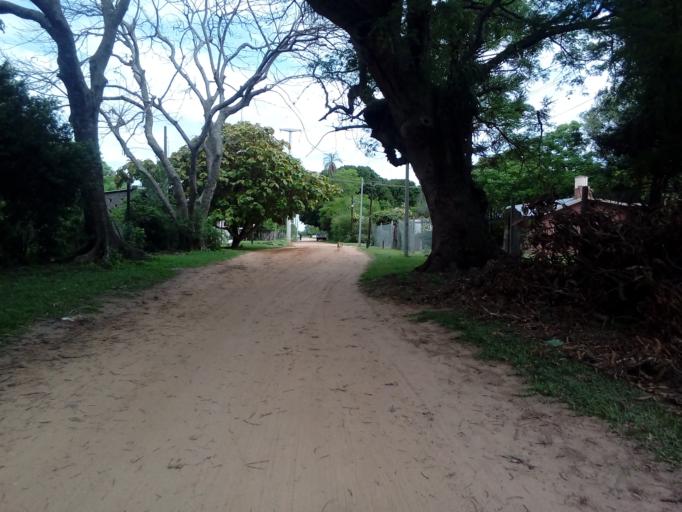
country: AR
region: Corrientes
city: San Luis del Palmar
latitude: -27.4591
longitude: -58.6523
